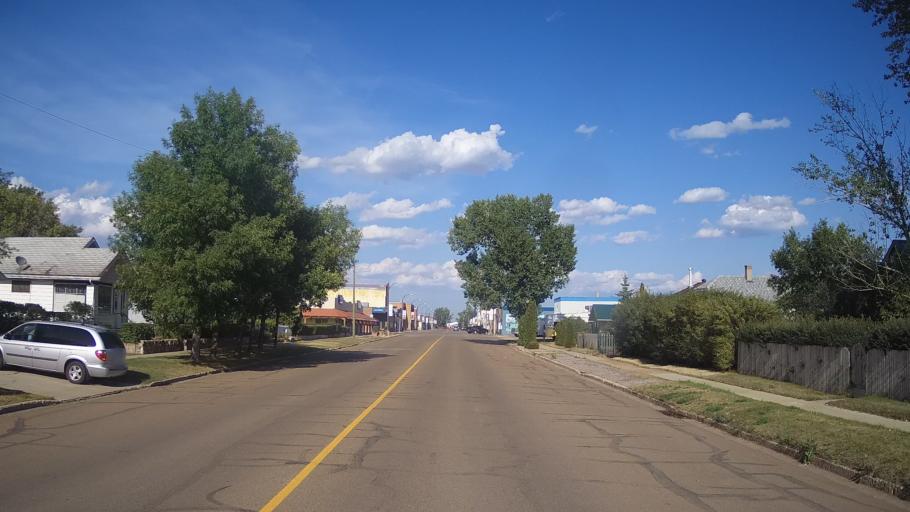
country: CA
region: Alberta
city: Hanna
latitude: 51.6422
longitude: -111.9324
